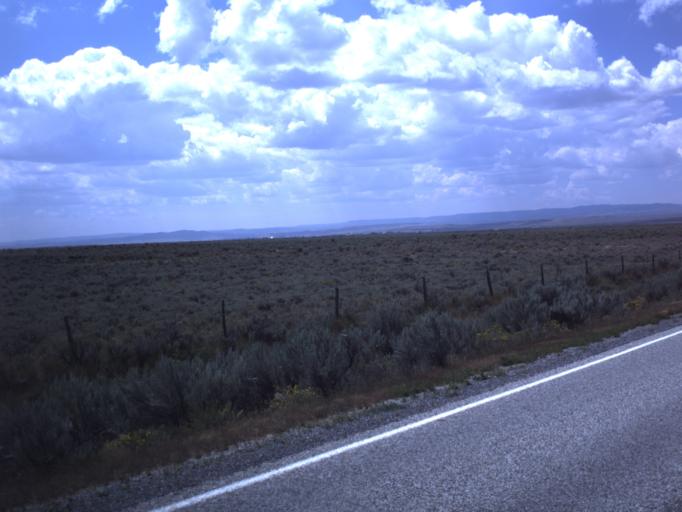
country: US
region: Utah
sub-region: Rich County
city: Randolph
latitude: 41.7786
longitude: -111.0575
